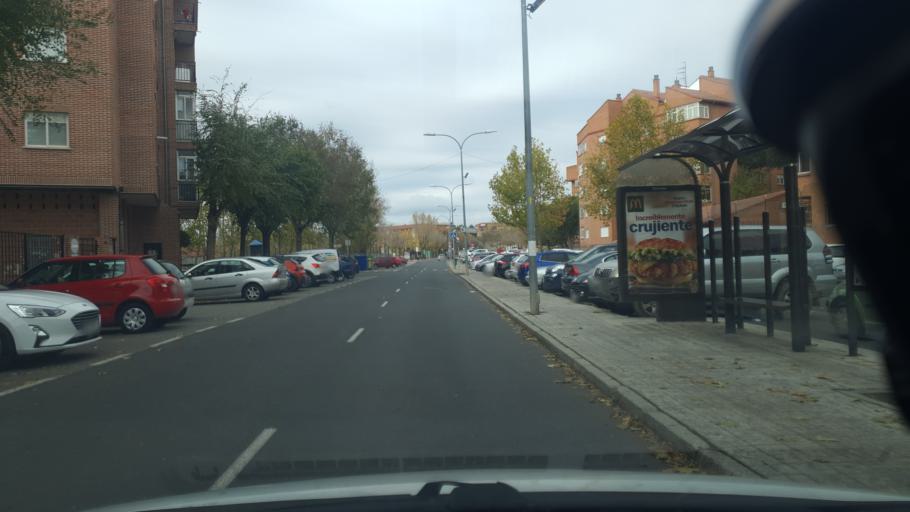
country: ES
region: Castille and Leon
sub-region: Provincia de Avila
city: Avila
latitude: 40.6467
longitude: -4.6845
